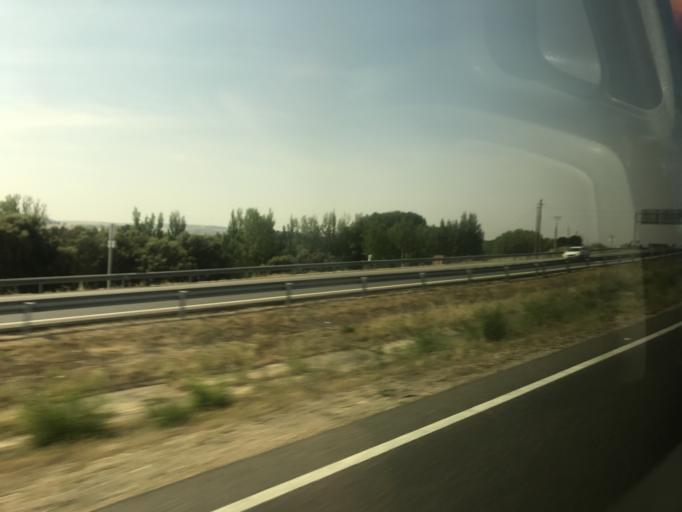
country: ES
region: Castille and Leon
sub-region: Provincia de Palencia
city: Quintana del Puente
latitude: 42.0986
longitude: -4.2015
